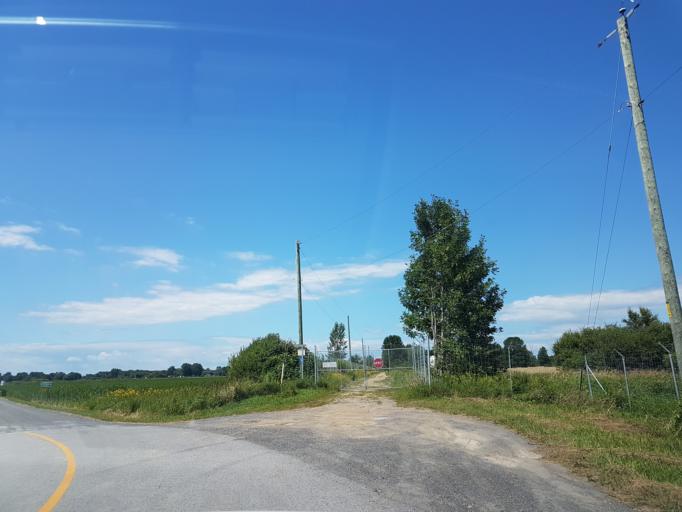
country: CA
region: Quebec
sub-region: Mauricie
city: Pierreville
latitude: 46.1524
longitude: -72.7421
